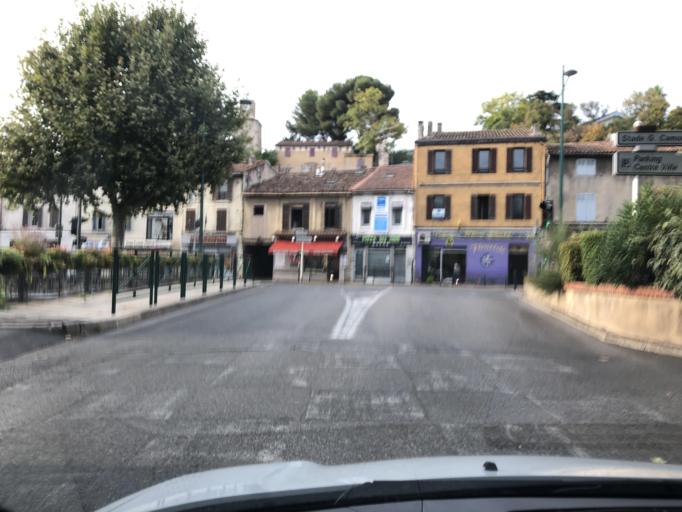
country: FR
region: Provence-Alpes-Cote d'Azur
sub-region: Departement des Bouches-du-Rhone
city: La Penne-sur-Huveaune
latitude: 43.2820
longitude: 5.5150
